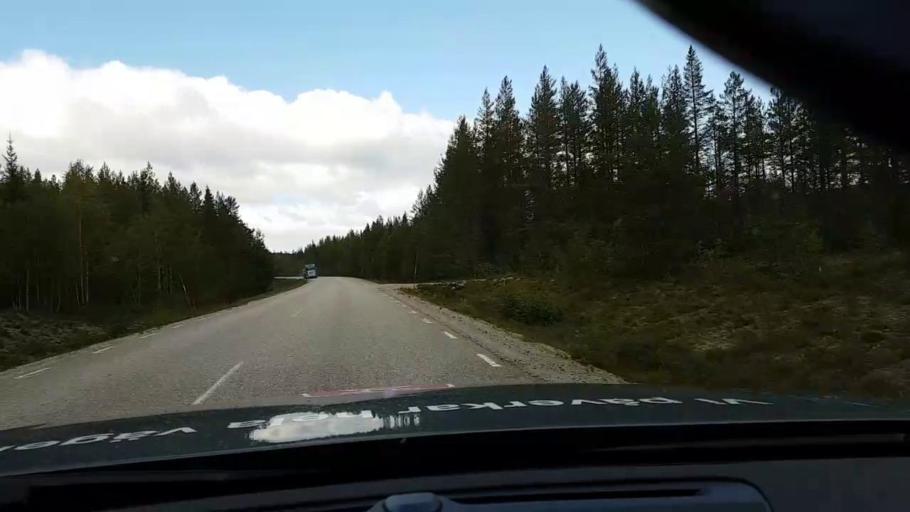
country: SE
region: Vaesterbotten
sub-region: Asele Kommun
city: Asele
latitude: 63.9243
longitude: 17.3181
